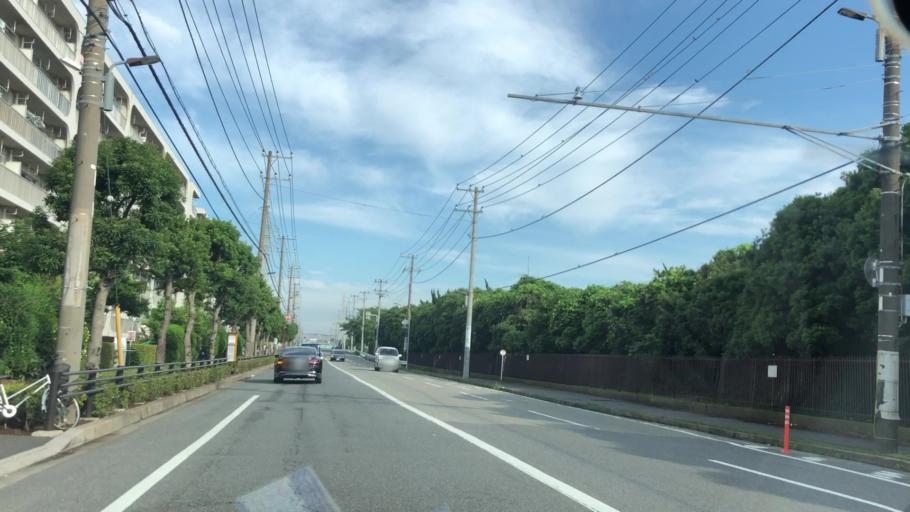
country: JP
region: Tokyo
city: Urayasu
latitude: 35.6757
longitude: 139.9219
